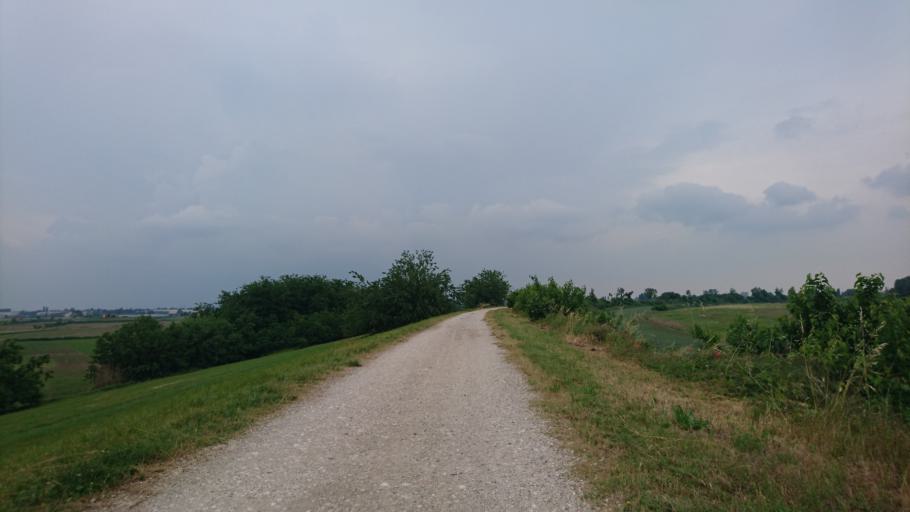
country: IT
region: Veneto
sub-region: Provincia di Padova
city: Masi
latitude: 45.1124
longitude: 11.5148
